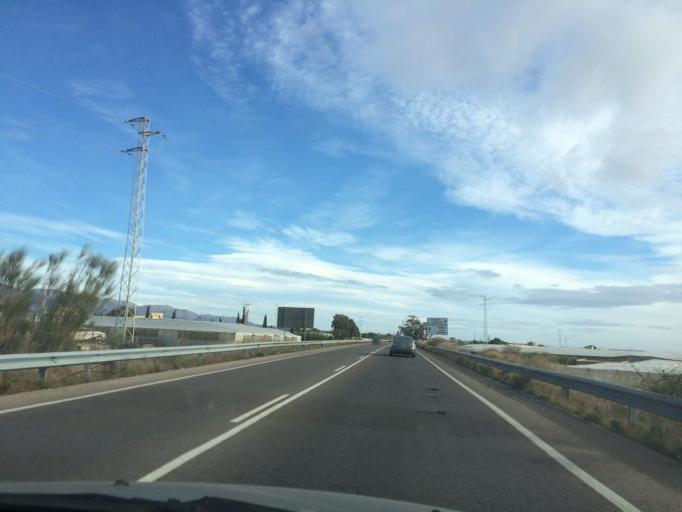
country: ES
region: Andalusia
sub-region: Provincia de Almeria
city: Retamar
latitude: 36.8541
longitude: -2.3696
